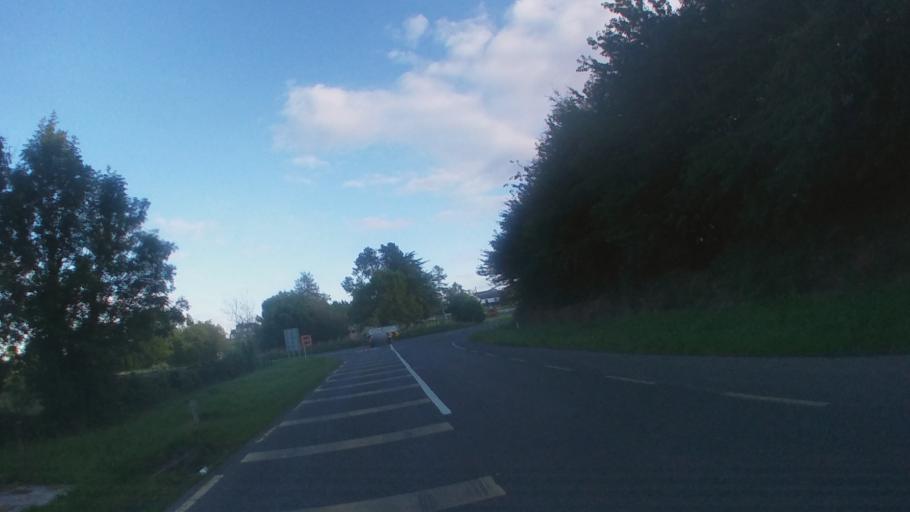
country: IE
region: Leinster
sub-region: Lu
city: Carlingford
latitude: 54.0210
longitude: -6.1459
